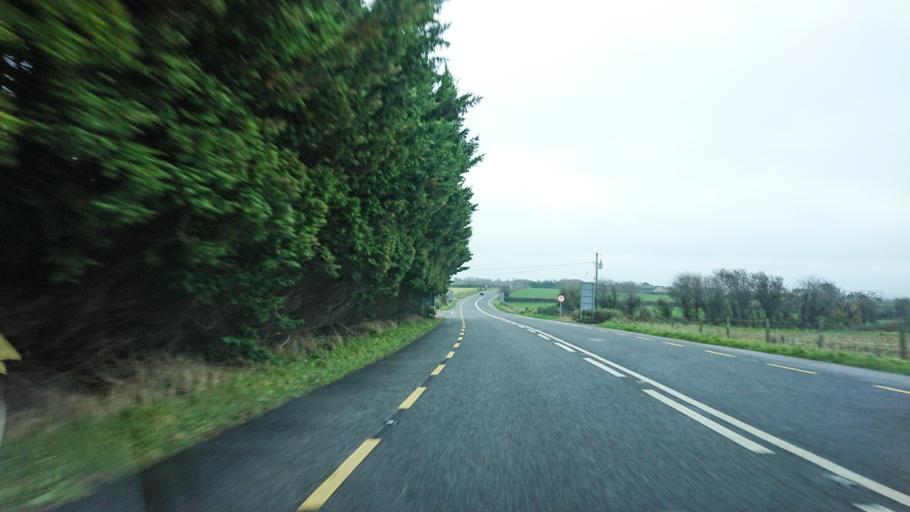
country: IE
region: Leinster
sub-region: Kilkenny
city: Mooncoin
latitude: 52.2904
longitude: -7.2409
